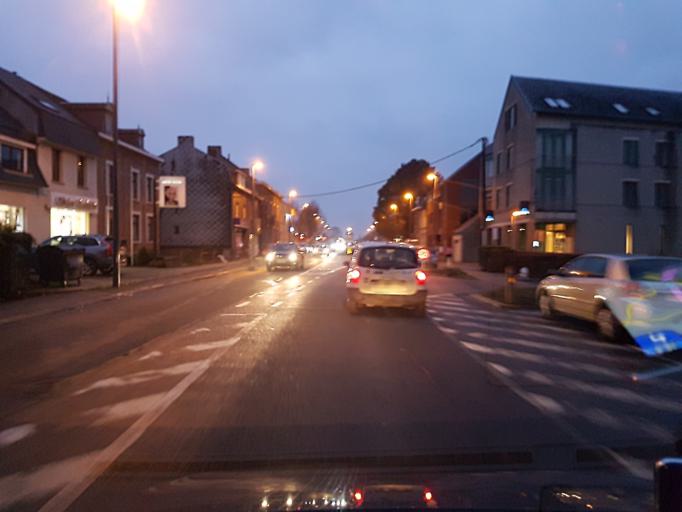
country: BE
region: Wallonia
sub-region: Province de Namur
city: Eghezee
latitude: 50.5932
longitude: 4.9109
